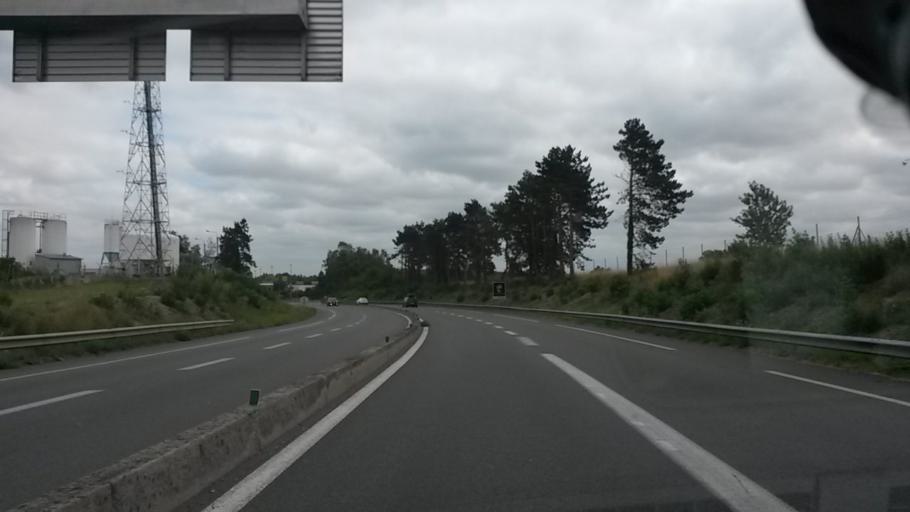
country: FR
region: Nord-Pas-de-Calais
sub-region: Departement du Nord
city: Raillencourt-Sainte-Olle
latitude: 50.1759
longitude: 3.1883
